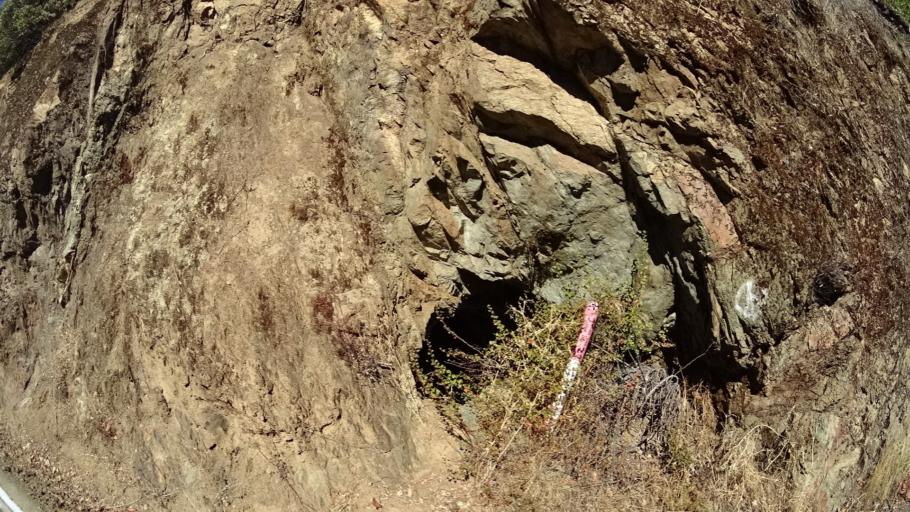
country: US
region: California
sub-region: Siskiyou County
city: Happy Camp
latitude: 41.3799
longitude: -123.4700
